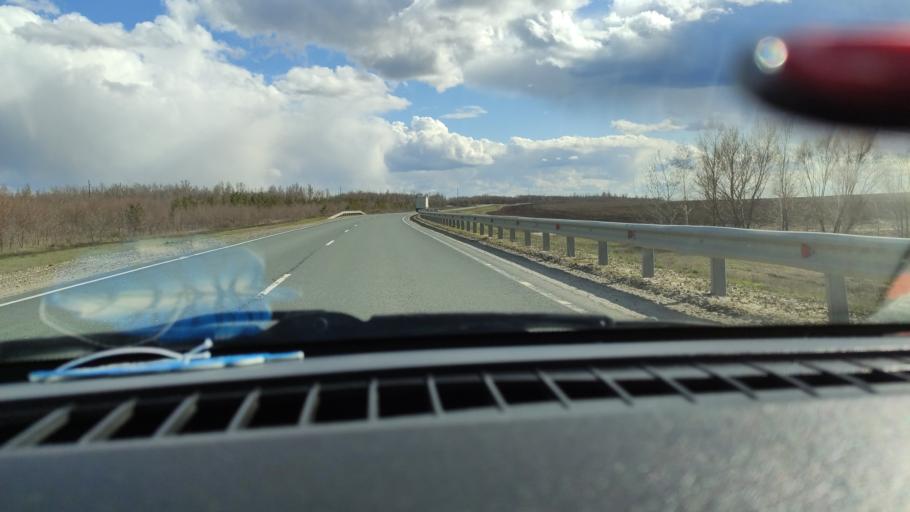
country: RU
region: Saratov
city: Alekseyevka
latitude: 52.2778
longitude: 47.9316
